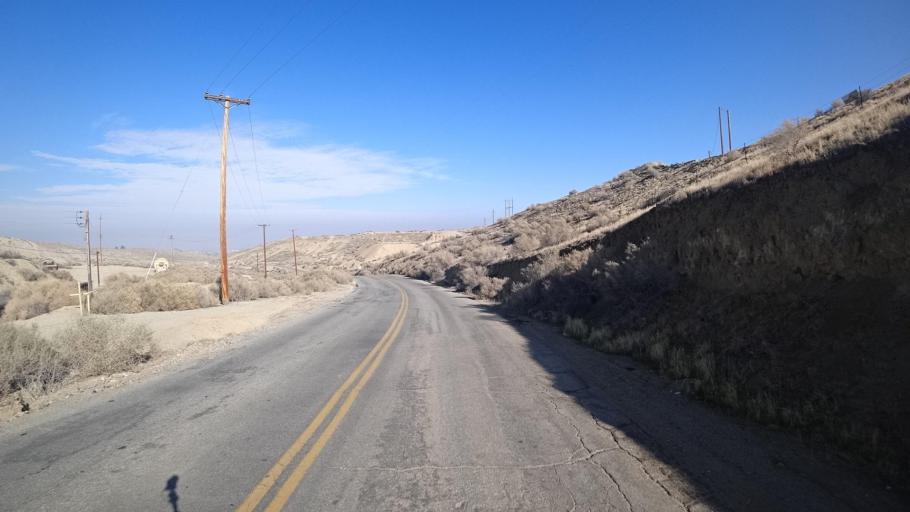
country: US
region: California
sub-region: Kern County
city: Taft Heights
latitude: 35.1212
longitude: -119.4728
